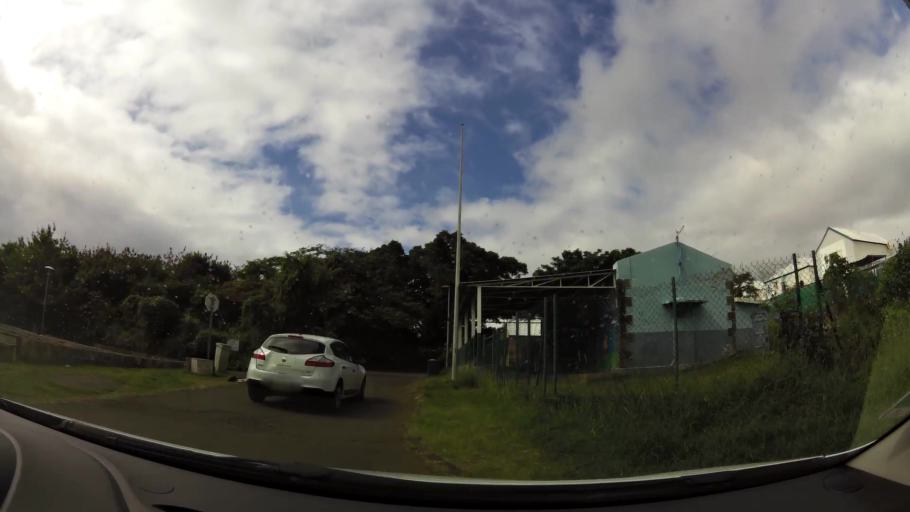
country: RE
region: Reunion
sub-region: Reunion
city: Sainte-Marie
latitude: -20.8945
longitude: 55.5653
